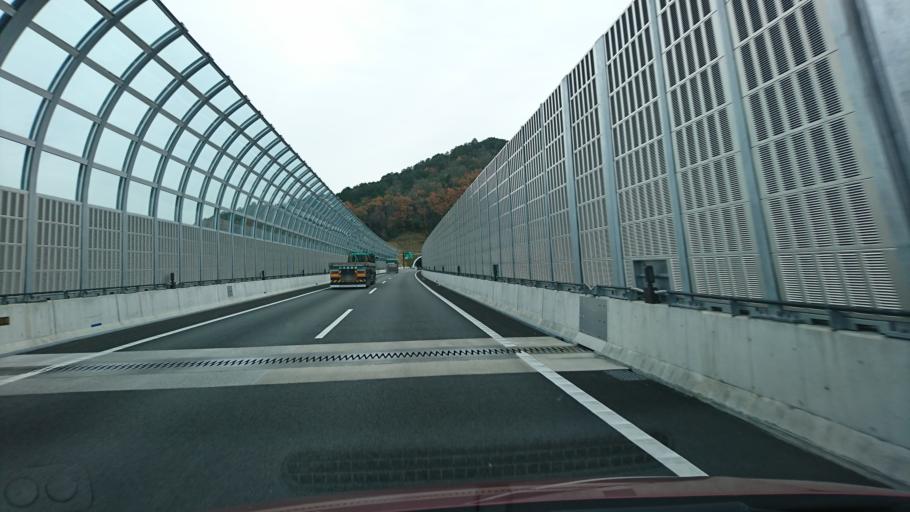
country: JP
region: Hyogo
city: Kawanishi
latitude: 34.8895
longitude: 135.3730
